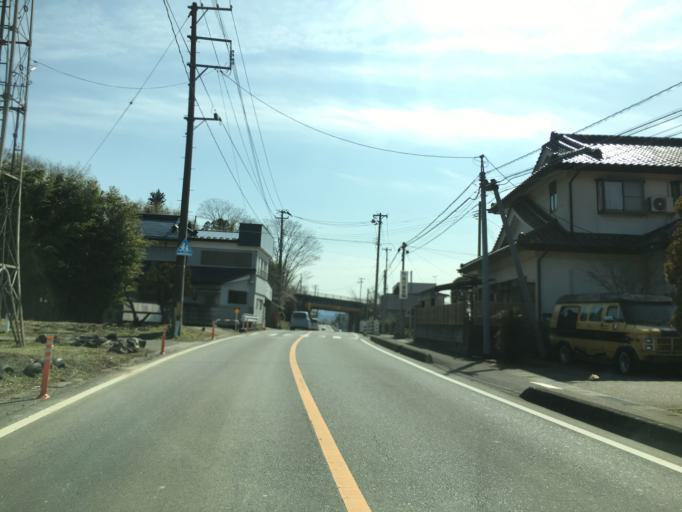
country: JP
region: Ibaraki
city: Daigo
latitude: 36.9165
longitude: 140.4168
